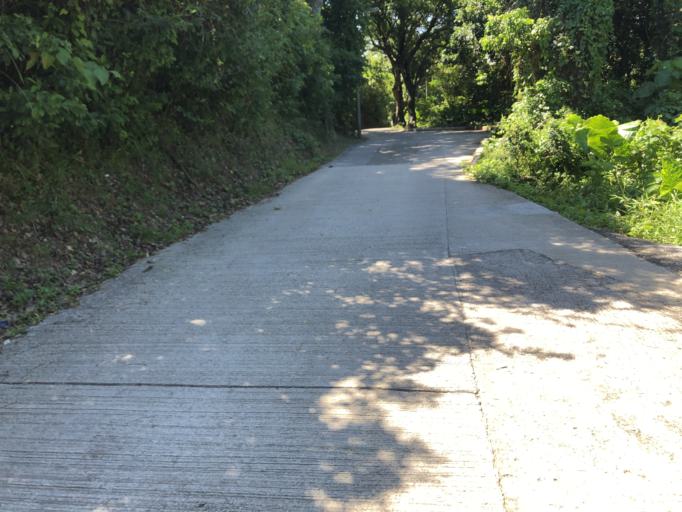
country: HK
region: Tuen Mun
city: Tuen Mun
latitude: 22.2965
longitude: 113.9700
